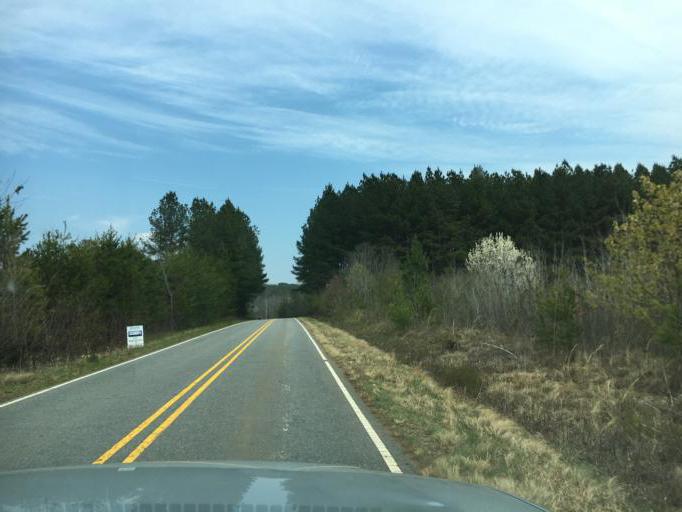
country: US
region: North Carolina
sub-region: Rutherford County
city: Lake Lure
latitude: 35.4554
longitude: -82.1369
